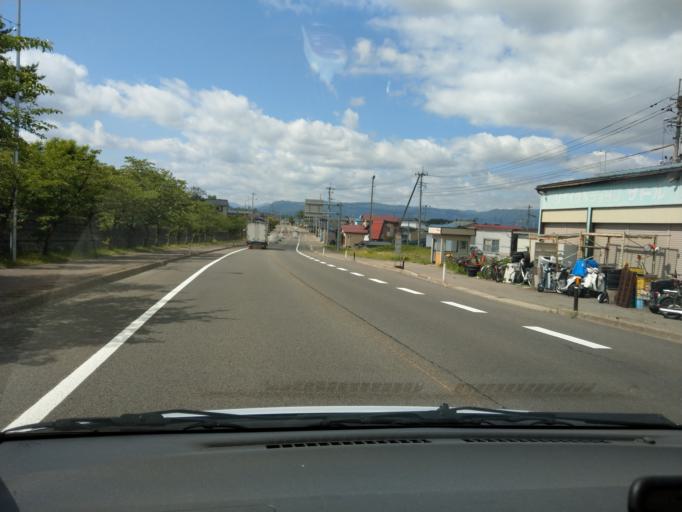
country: JP
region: Akita
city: Yuzawa
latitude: 39.2005
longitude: 140.5059
